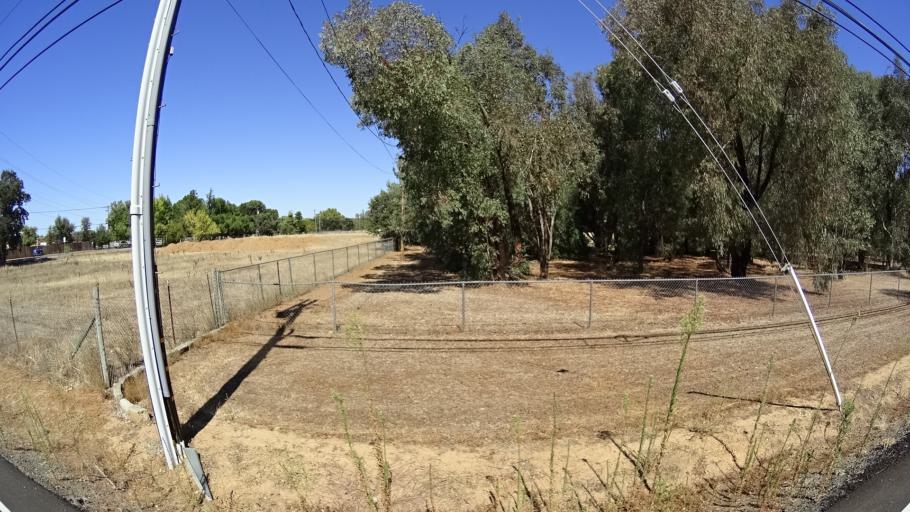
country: US
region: California
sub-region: Sacramento County
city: Vineyard
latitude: 38.4382
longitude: -121.3243
